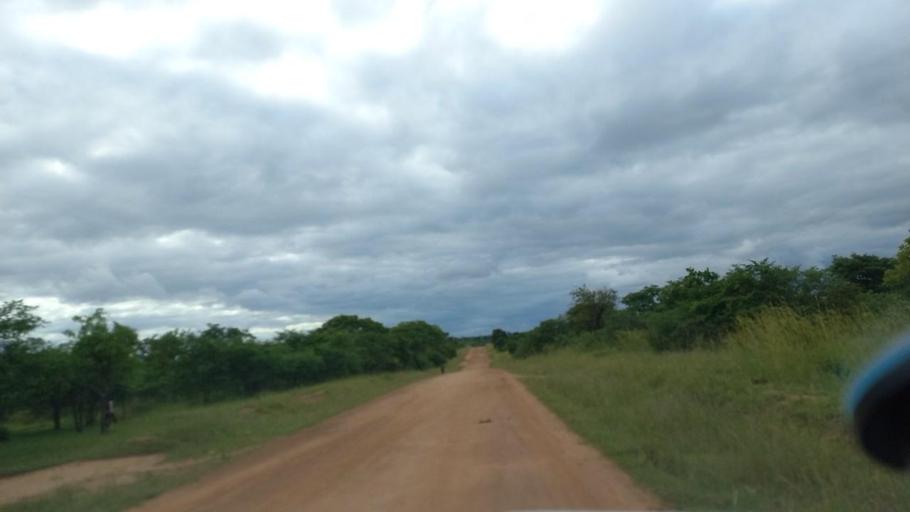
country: ZM
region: Lusaka
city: Chongwe
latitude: -15.4513
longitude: 28.8490
